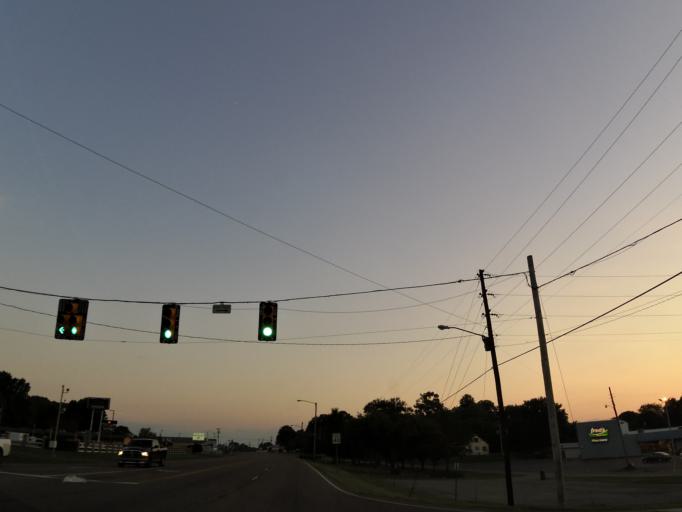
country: US
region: Tennessee
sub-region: Carroll County
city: McKenzie
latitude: 36.1239
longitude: -88.5173
